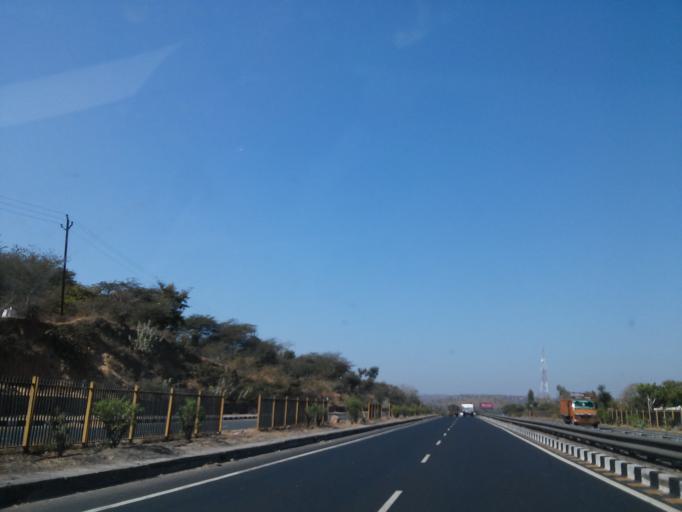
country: IN
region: Gujarat
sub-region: Sabar Kantha
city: Modasa
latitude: 23.6031
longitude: 73.1792
